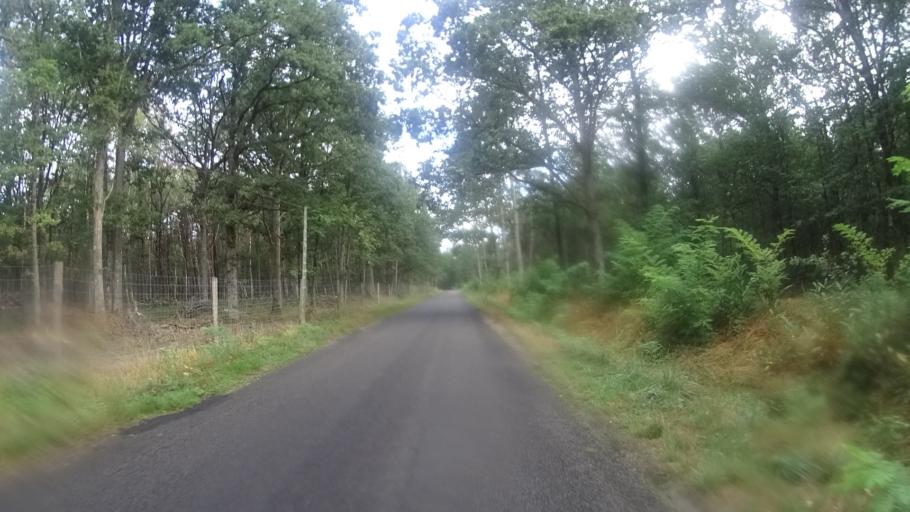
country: FR
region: Centre
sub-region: Departement du Loiret
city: Chateauneuf-sur-Loire
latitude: 47.9035
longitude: 2.2103
